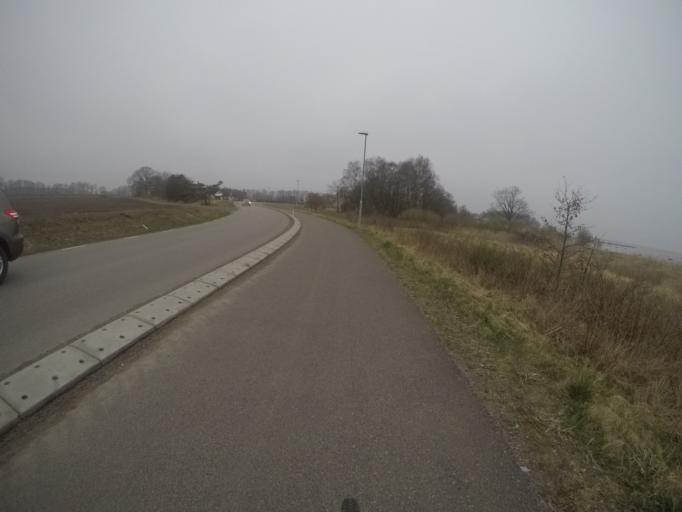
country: SE
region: Skane
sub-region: Angelholms Kommun
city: Strovelstorp
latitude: 56.2189
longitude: 12.7664
